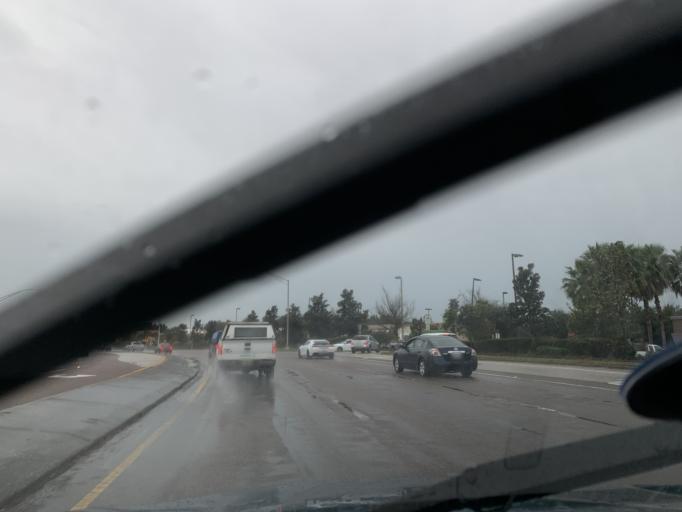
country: US
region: Florida
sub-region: Pasco County
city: Jasmine Estates
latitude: 28.2799
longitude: -82.6760
